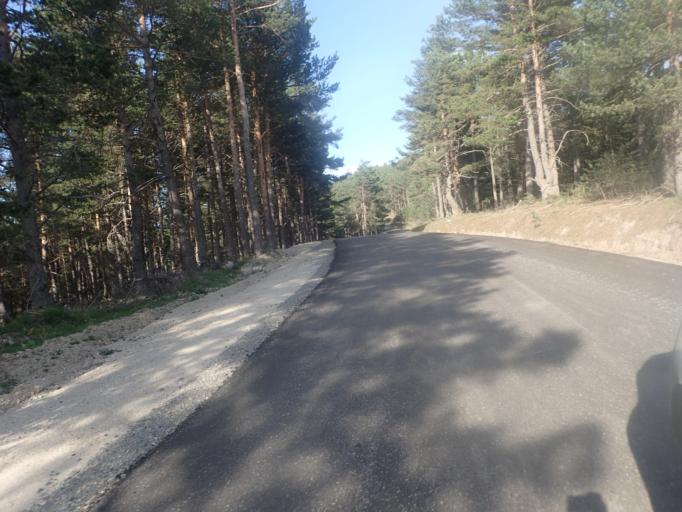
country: TR
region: Ordu
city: Mesudiye
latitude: 40.4010
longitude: 37.8477
